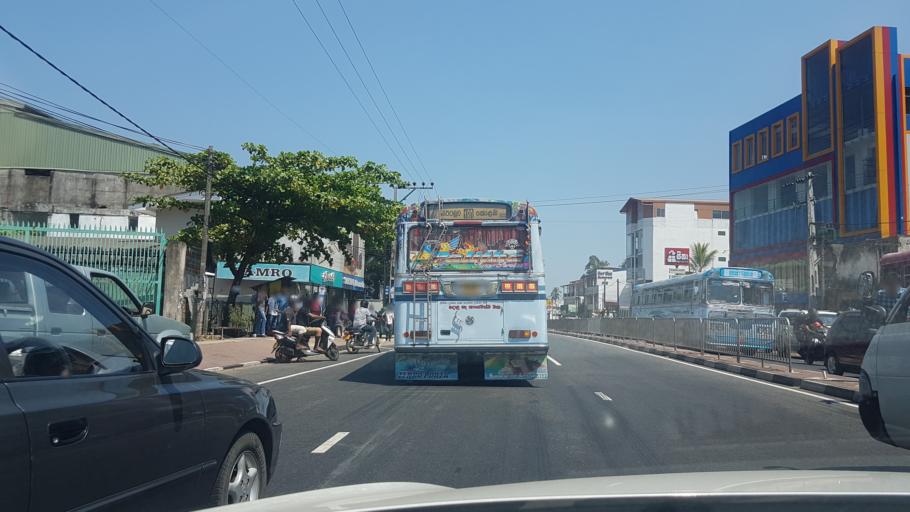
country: LK
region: Western
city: Gampaha
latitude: 7.0869
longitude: 80.0344
